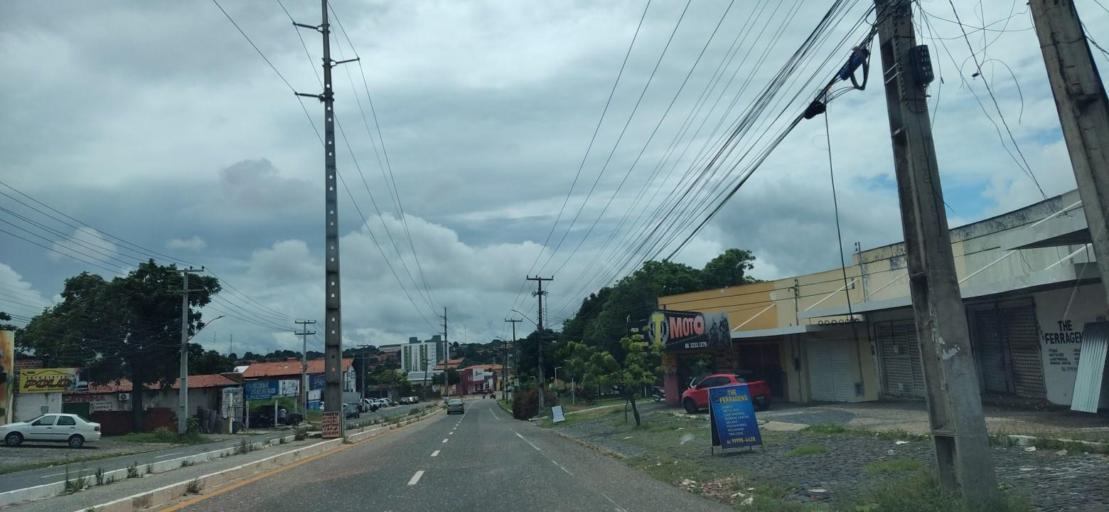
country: BR
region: Piaui
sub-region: Teresina
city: Teresina
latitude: -5.0614
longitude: -42.7563
